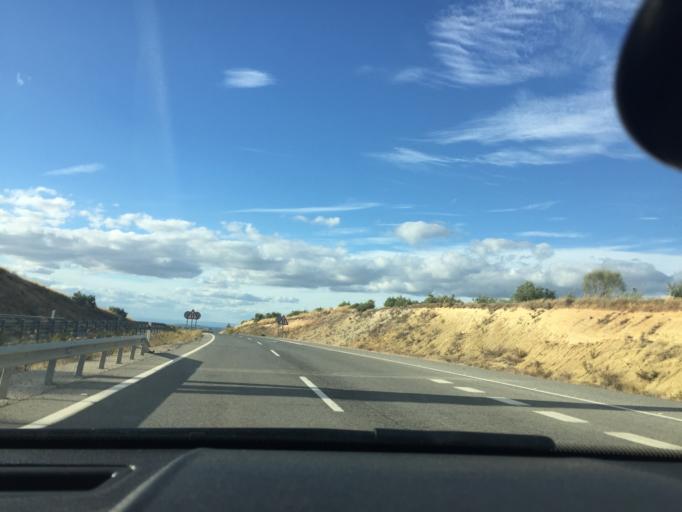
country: ES
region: Andalusia
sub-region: Provincia de Jaen
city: Torredonjimeno
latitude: 37.7550
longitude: -3.9598
